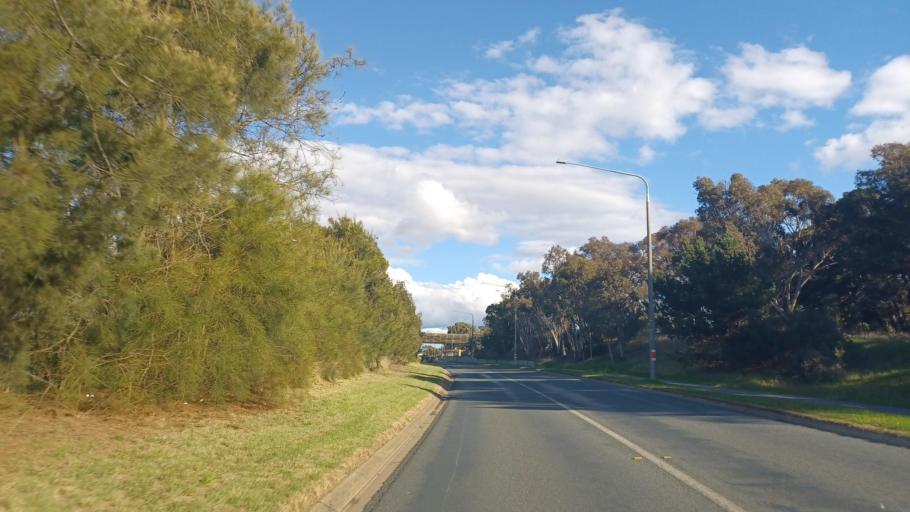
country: AU
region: Australian Capital Territory
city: Belconnen
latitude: -35.1869
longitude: 149.0724
